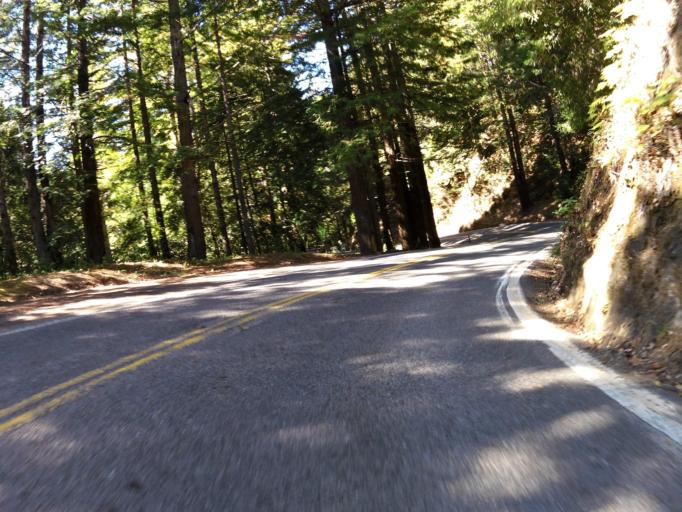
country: US
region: California
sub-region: Humboldt County
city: Redway
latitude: 39.7946
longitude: -123.8137
